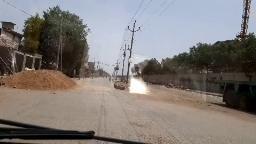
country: PK
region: Sindh
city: Malir Cantonment
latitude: 24.8391
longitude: 67.2045
